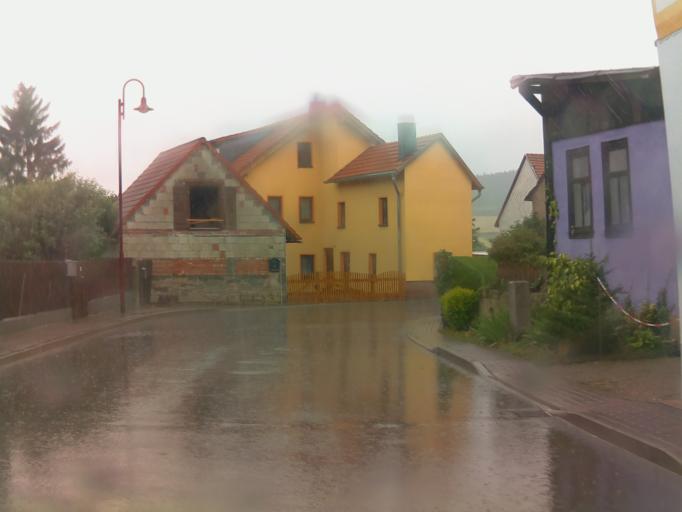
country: DE
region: Thuringia
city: Stadtilm
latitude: 50.7525
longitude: 11.1201
